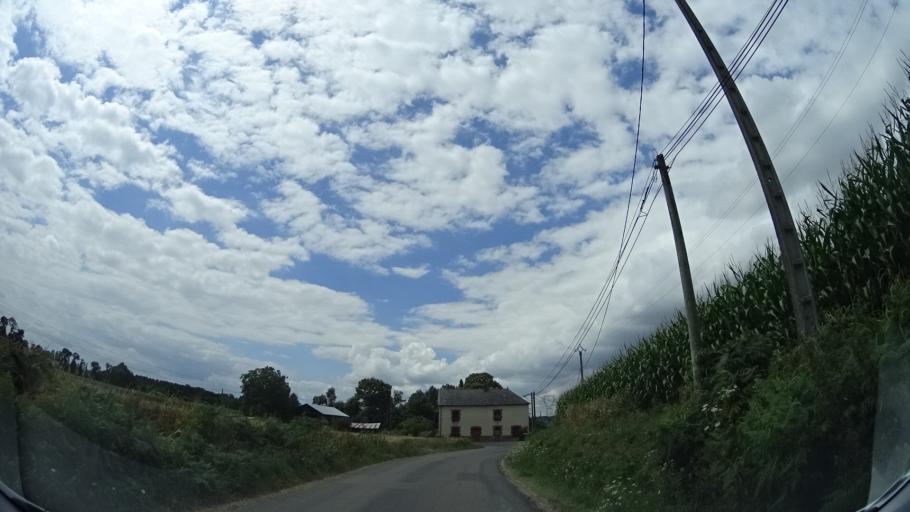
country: FR
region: Brittany
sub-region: Departement d'Ille-et-Vilaine
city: La Meziere
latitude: 48.1943
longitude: -1.7670
